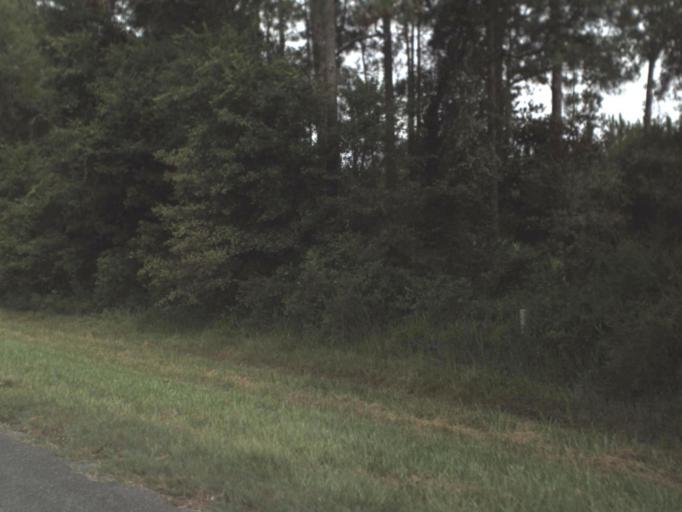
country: US
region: Florida
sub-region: Taylor County
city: Perry
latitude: 30.0993
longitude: -83.4630
